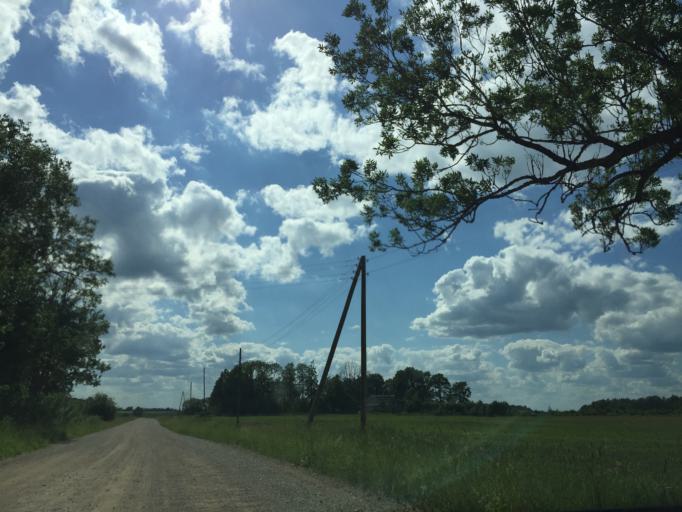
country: LV
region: Tukuma Rajons
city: Tukums
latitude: 56.9006
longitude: 23.1200
